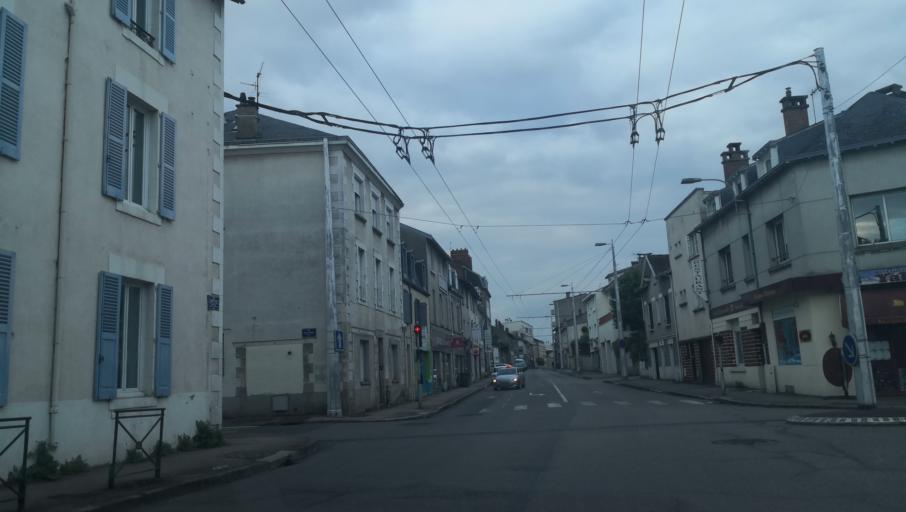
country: FR
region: Limousin
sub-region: Departement de la Haute-Vienne
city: Limoges
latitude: 45.8272
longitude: 1.2394
